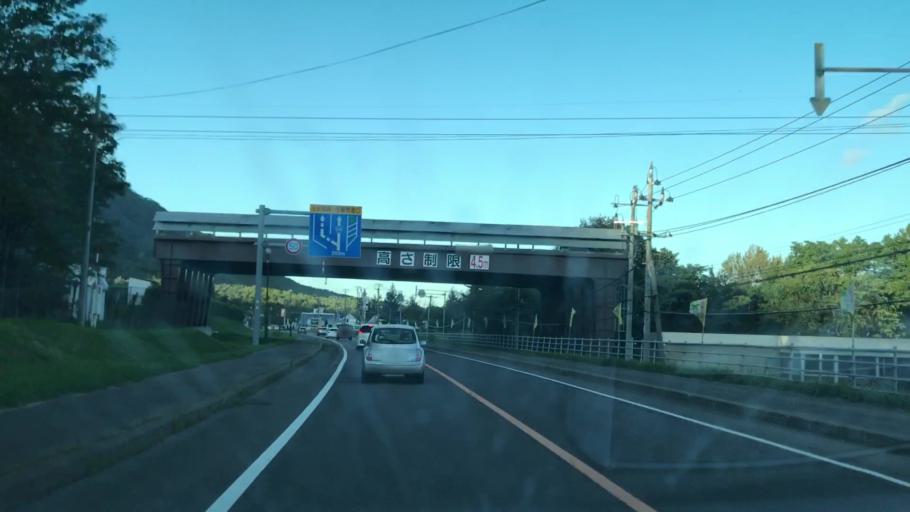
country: JP
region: Hokkaido
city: Niseko Town
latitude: 42.7482
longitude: 140.9002
